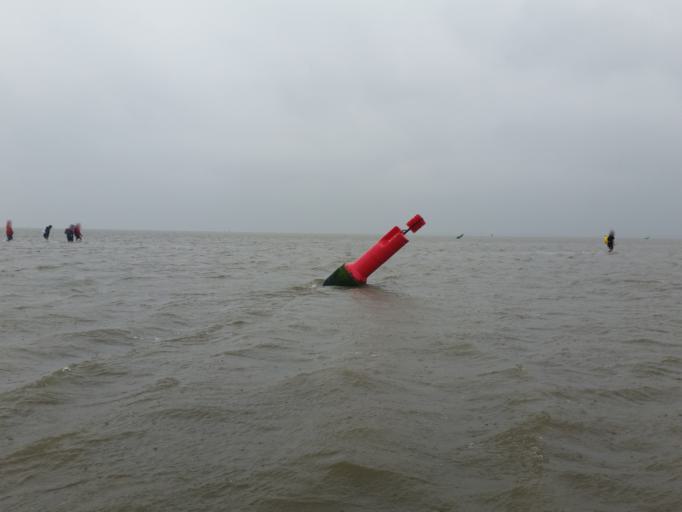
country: NL
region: Friesland
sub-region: Gemeente Dongeradeel
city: Holwerd
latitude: 53.4230
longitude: 5.9084
